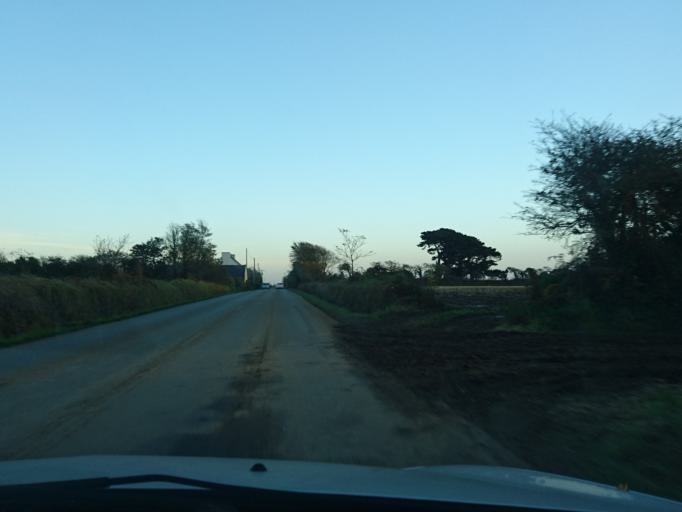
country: FR
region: Brittany
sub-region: Departement du Finistere
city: Lanrivoare
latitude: 48.4620
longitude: -4.6343
